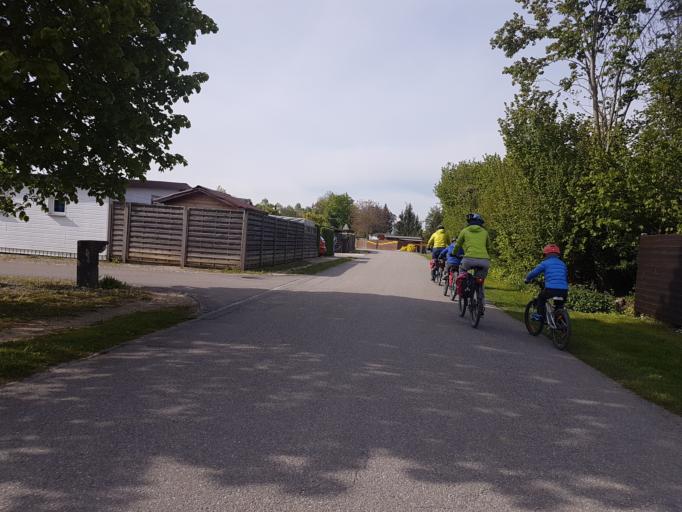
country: CH
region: Bern
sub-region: Biel/Bienne District
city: Bellmund
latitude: 47.1088
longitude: 7.2191
